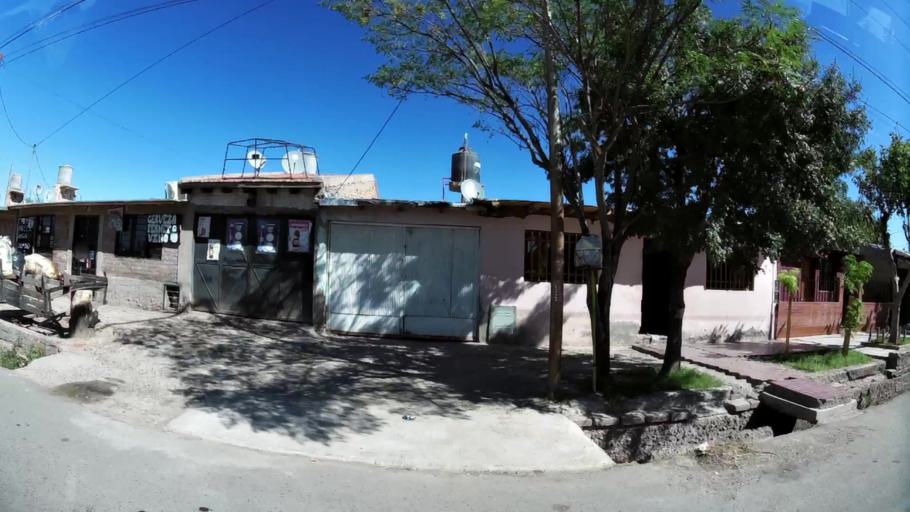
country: AR
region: Mendoza
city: Las Heras
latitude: -32.8285
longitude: -68.8193
